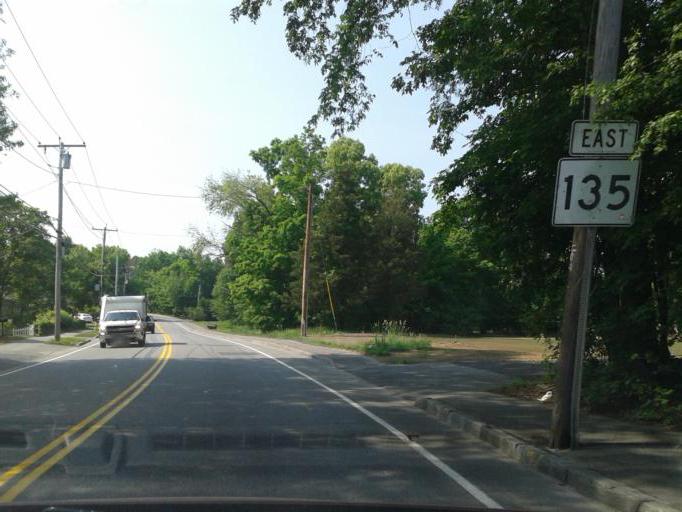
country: US
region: Massachusetts
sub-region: Worcester County
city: Westborough
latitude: 42.2619
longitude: -71.6102
